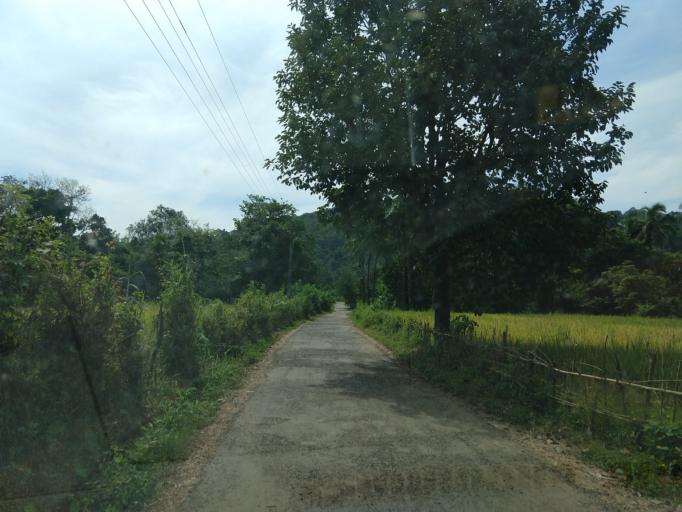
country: IN
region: Maharashtra
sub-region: Sindhudurg
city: Savantvadi
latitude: 15.9748
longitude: 73.7870
